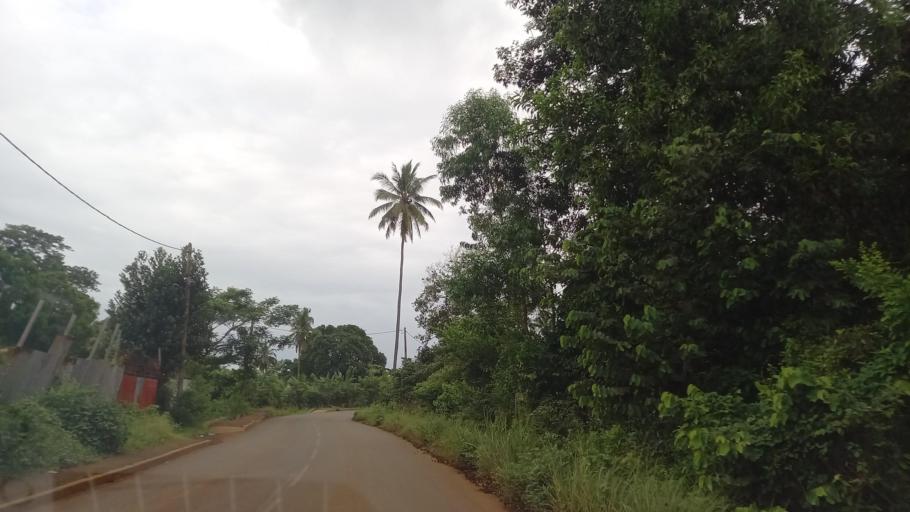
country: YT
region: Chiconi
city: Chiconi
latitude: -12.8293
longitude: 45.1272
